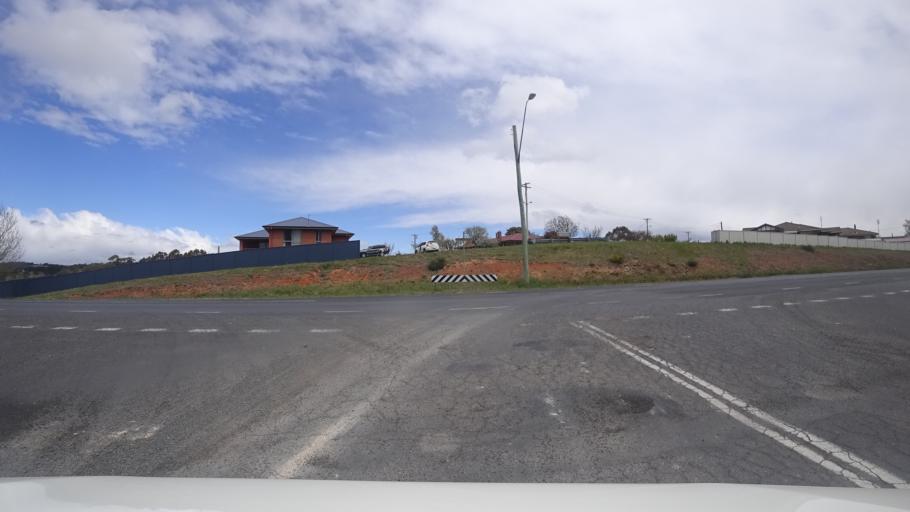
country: AU
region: New South Wales
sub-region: Oberon
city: Oberon
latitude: -33.7014
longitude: 149.8759
